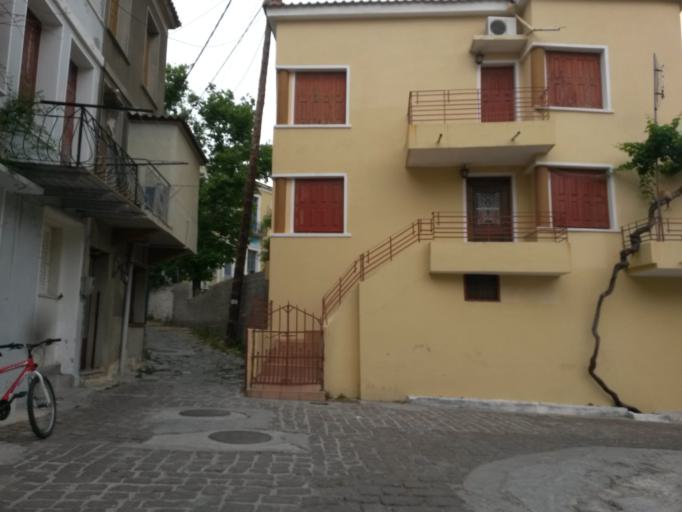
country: GR
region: North Aegean
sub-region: Nomos Lesvou
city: Plomarion
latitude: 38.9773
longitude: 26.3702
